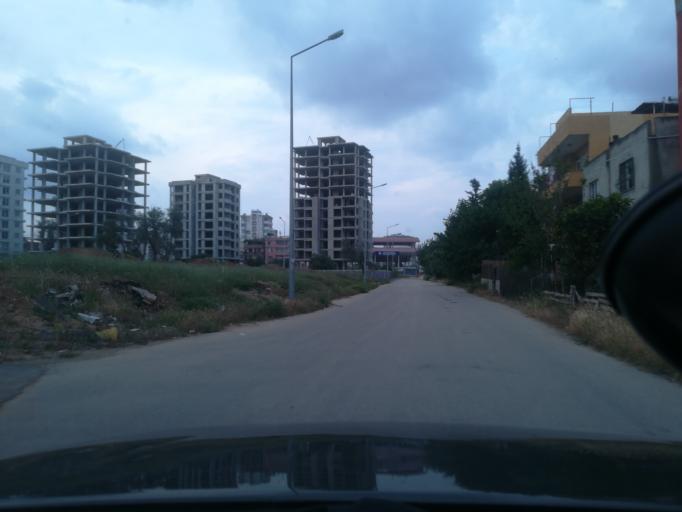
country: TR
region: Adana
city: Seyhan
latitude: 37.0158
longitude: 35.2705
